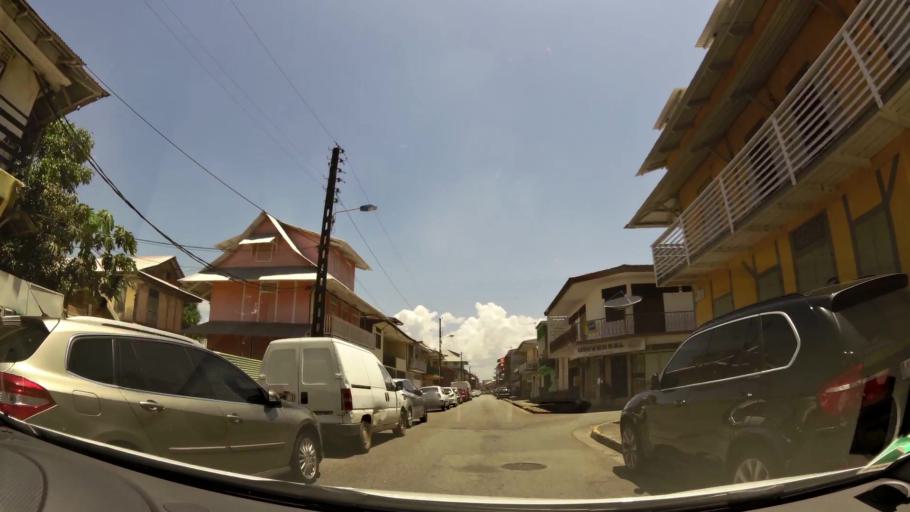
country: GF
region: Guyane
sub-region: Guyane
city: Cayenne
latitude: 4.9382
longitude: -52.3289
